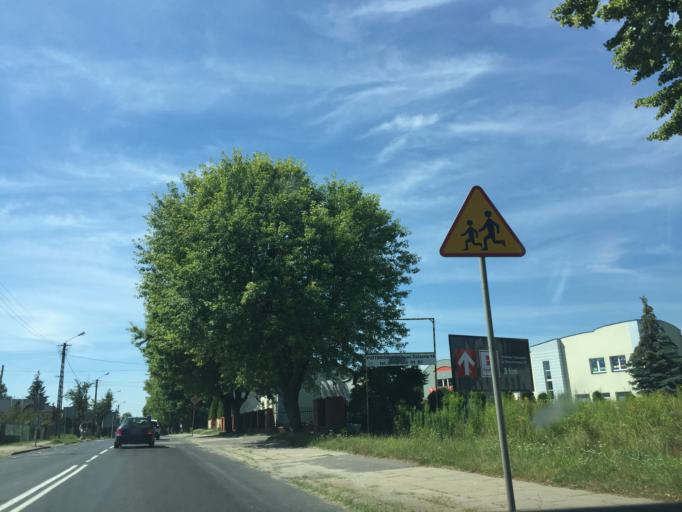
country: PL
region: Lodz Voivodeship
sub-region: Piotrkow Trybunalski
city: Piotrkow Trybunalski
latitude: 51.4152
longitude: 19.7120
